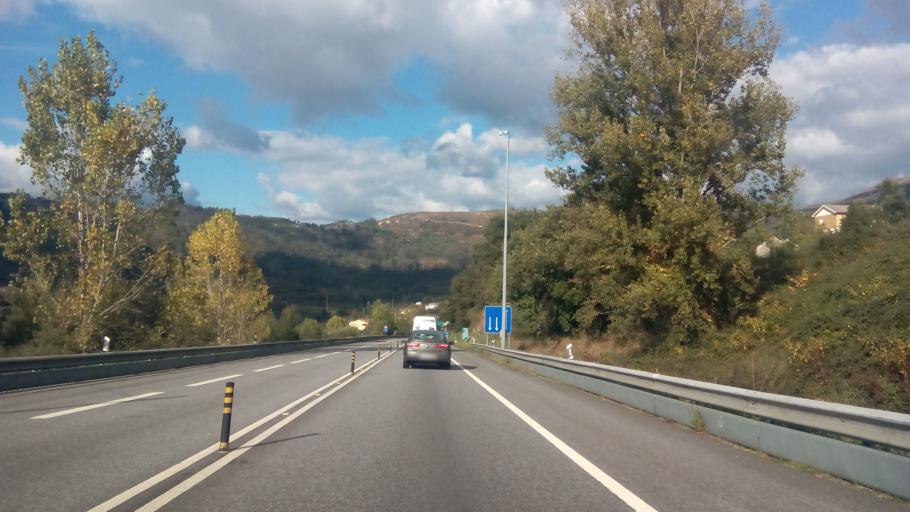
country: PT
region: Porto
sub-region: Amarante
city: Amarante
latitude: 41.2749
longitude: -7.9921
